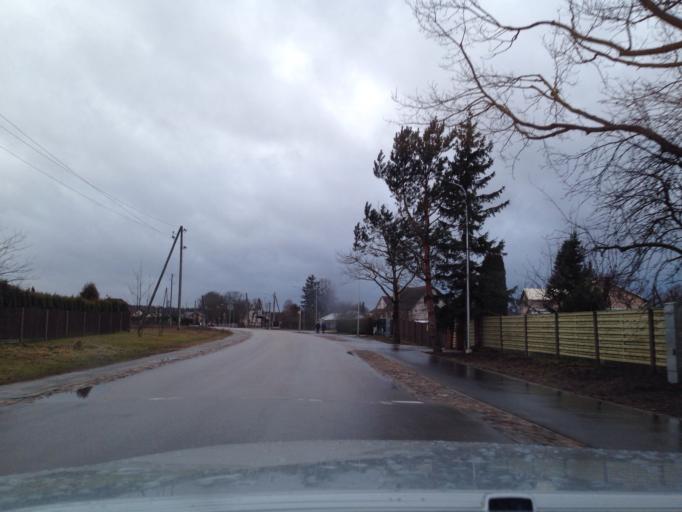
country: LV
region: Marupe
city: Marupe
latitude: 56.8944
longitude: 24.0420
